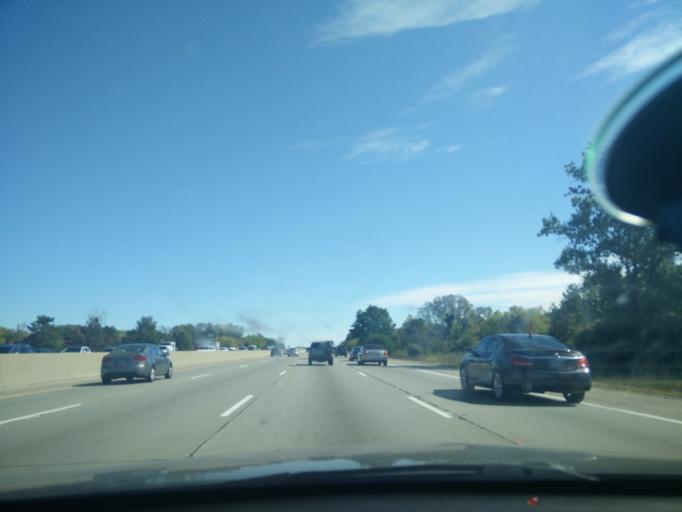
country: US
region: Michigan
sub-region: Oakland County
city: Farmington Hills
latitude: 42.4953
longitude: -83.3724
